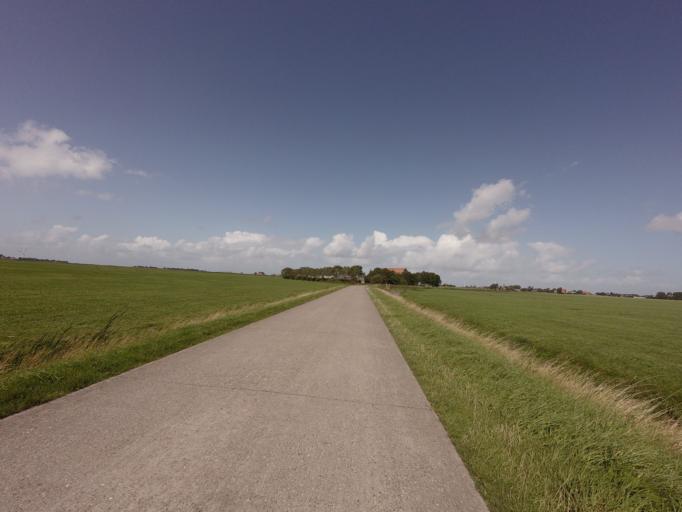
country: NL
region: Friesland
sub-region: Sudwest Fryslan
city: Makkum
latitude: 53.0685
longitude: 5.4557
